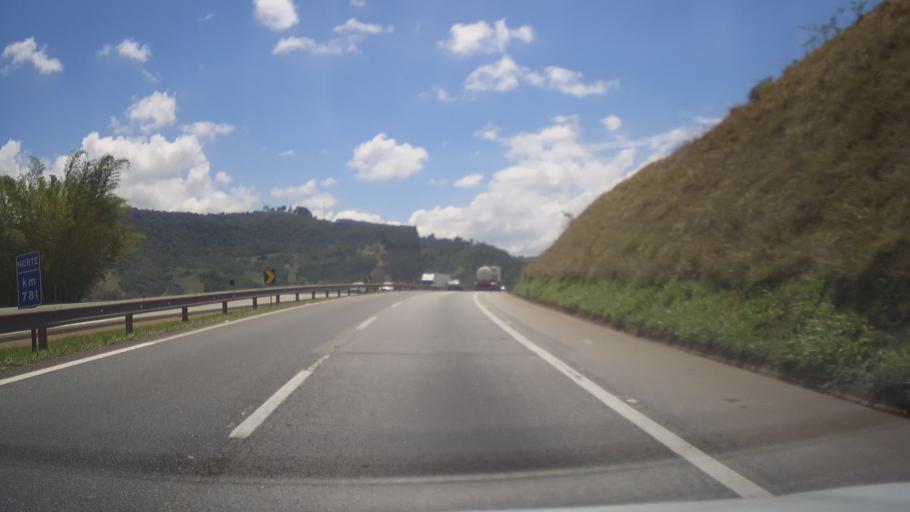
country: BR
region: Minas Gerais
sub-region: Campanha
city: Campanha
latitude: -21.8169
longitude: -45.4926
